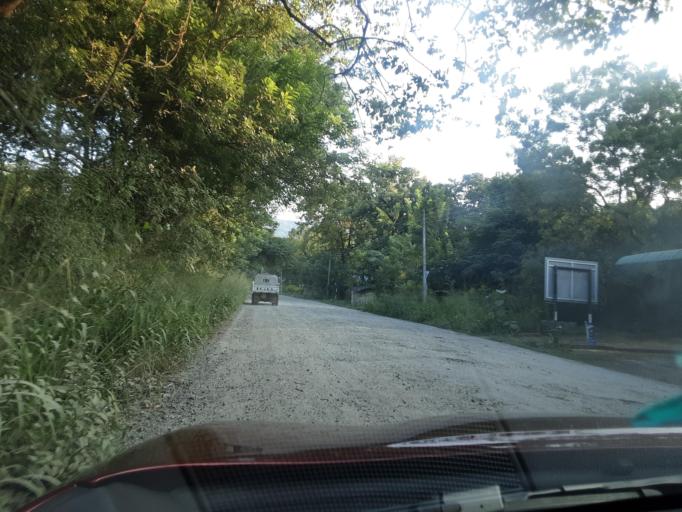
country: LK
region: Central
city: Dambulla
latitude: 7.8576
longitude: 80.6816
